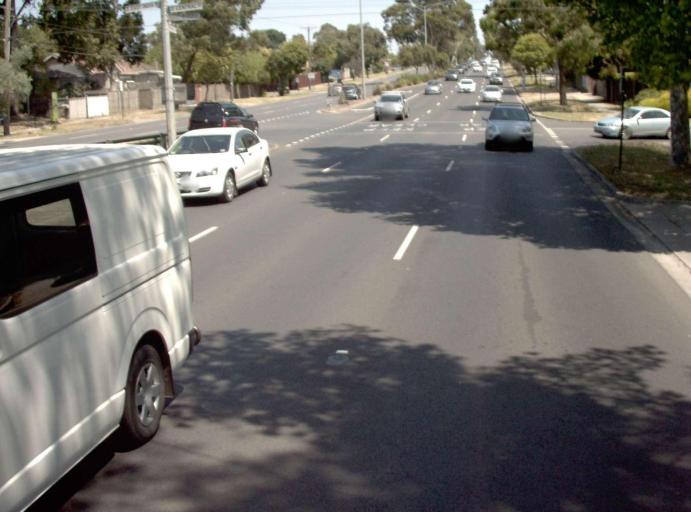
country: AU
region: Victoria
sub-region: Whitehorse
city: Nunawading
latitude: -37.8243
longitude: 145.1747
